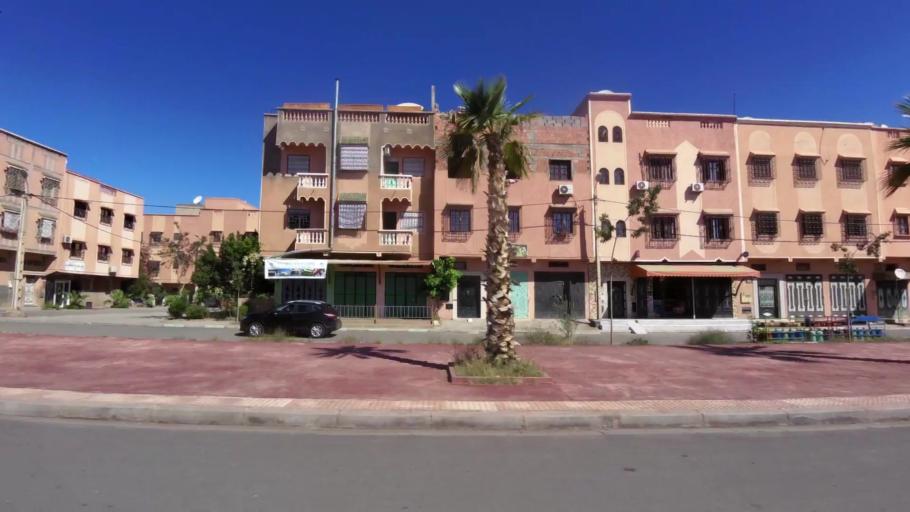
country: MA
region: Marrakech-Tensift-Al Haouz
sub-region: Marrakech
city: Marrakesh
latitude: 31.5931
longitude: -8.0453
